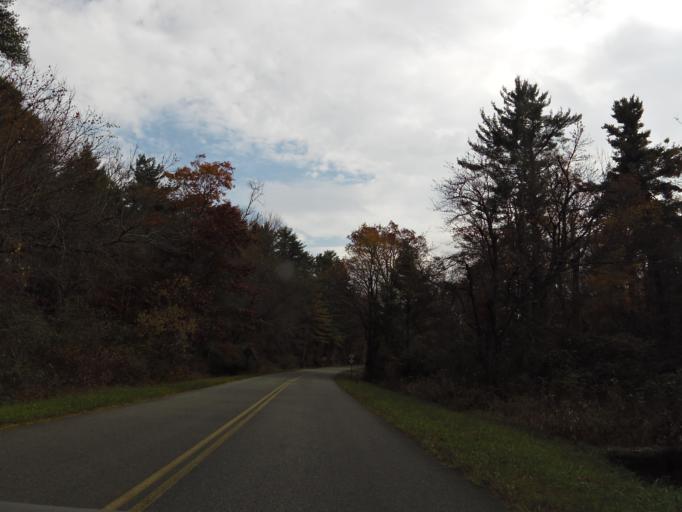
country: US
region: Virginia
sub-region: City of Galax
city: Galax
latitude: 36.5607
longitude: -80.9122
